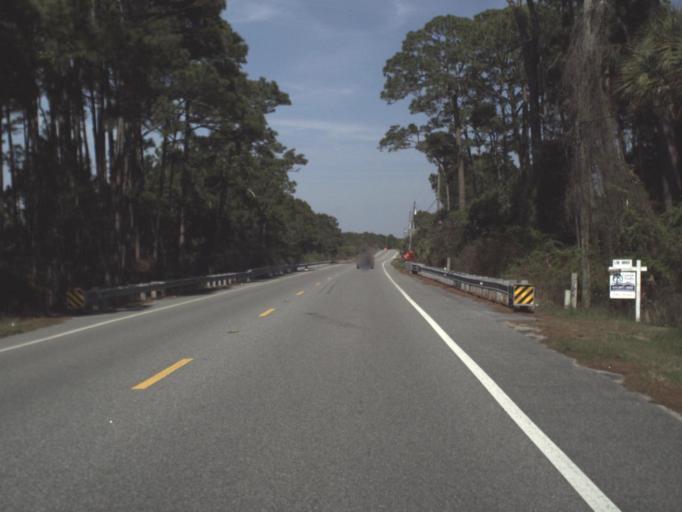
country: US
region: Florida
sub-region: Franklin County
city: Carrabelle
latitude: 29.7974
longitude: -84.7459
